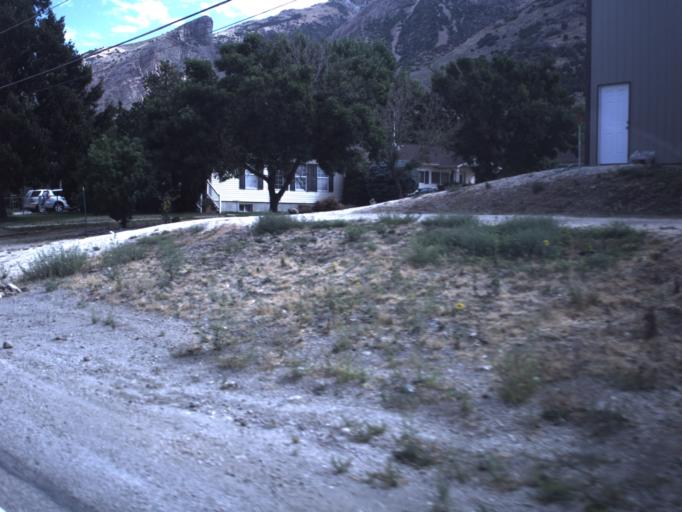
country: US
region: Utah
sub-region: Box Elder County
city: Willard
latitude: 41.3948
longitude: -112.0342
